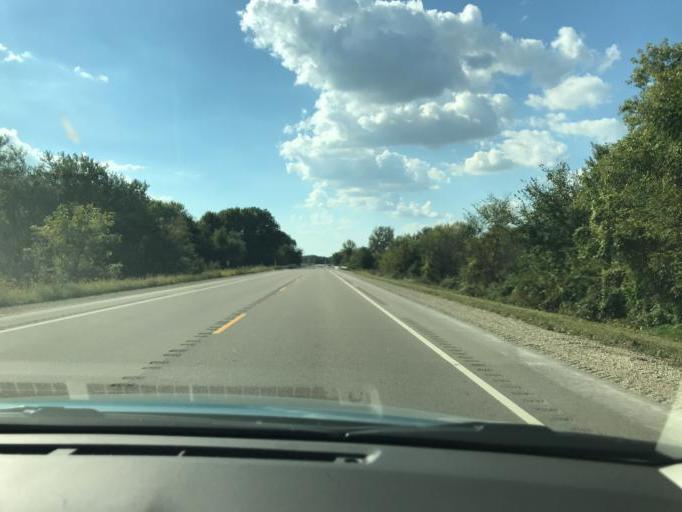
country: US
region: Wisconsin
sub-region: Green County
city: Brodhead
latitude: 42.5733
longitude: -89.3589
